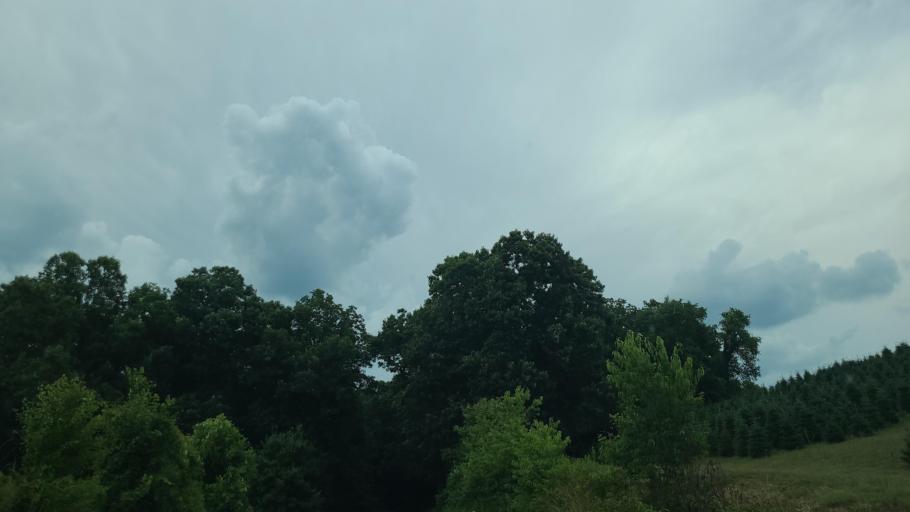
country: US
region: North Carolina
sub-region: Ashe County
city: Jefferson
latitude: 36.3972
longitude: -81.4058
